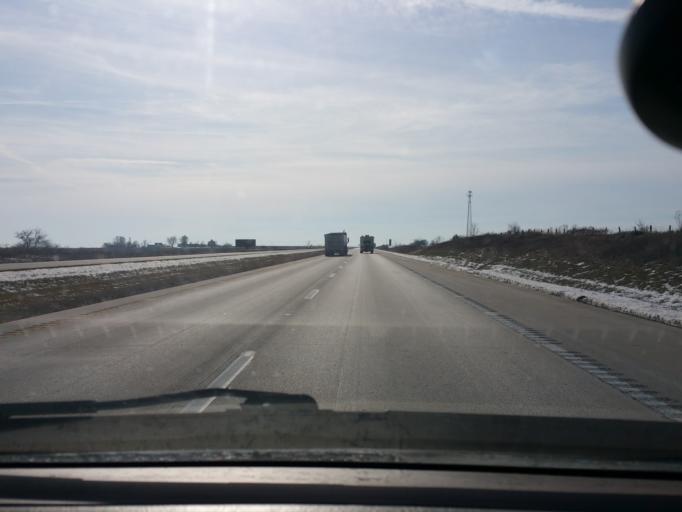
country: US
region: Missouri
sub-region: Clinton County
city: Lathrop
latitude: 39.5811
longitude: -94.2593
